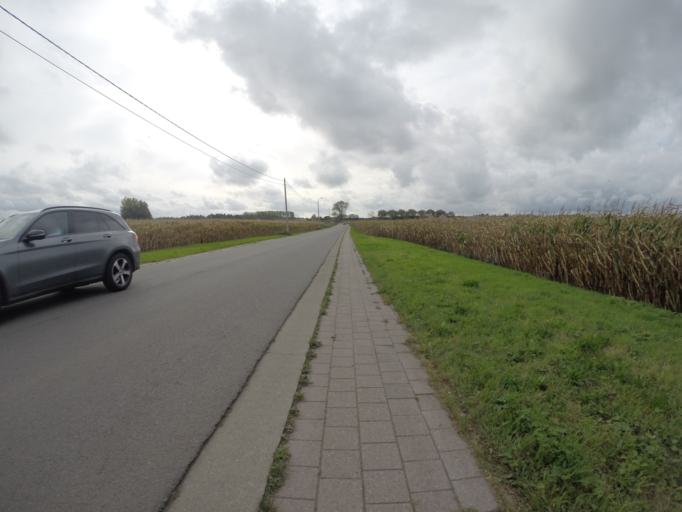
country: BE
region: Flanders
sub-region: Provincie Oost-Vlaanderen
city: Knesselare
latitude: 51.1162
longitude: 3.3911
